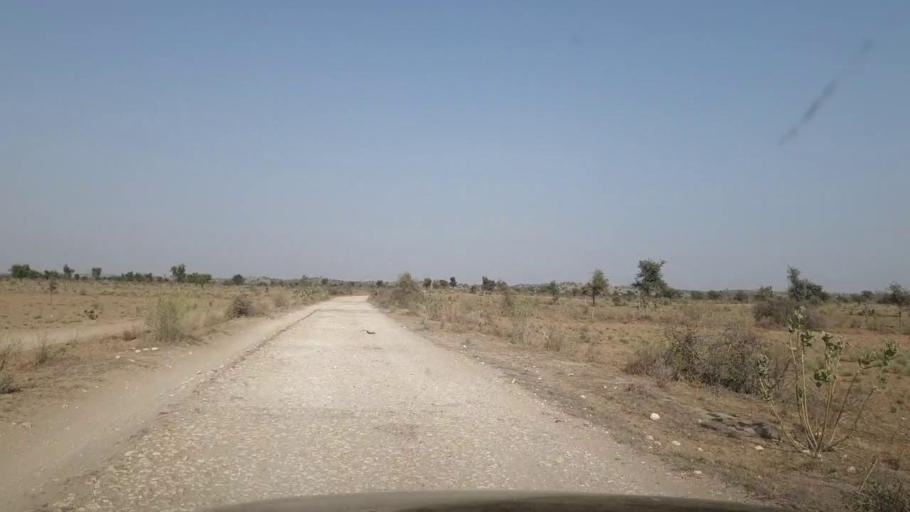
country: PK
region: Sindh
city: Islamkot
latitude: 25.0991
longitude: 70.4018
